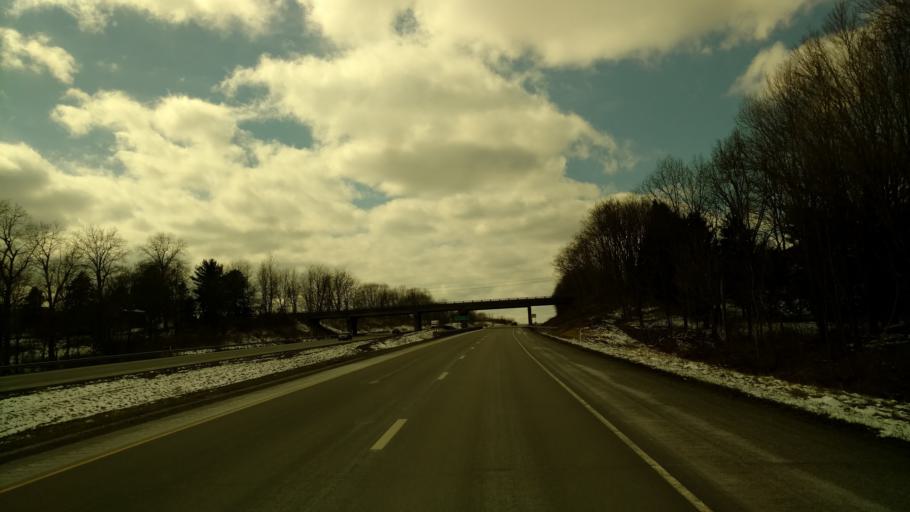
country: US
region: Pennsylvania
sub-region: Mercer County
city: Hermitage
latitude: 41.1831
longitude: -80.3919
